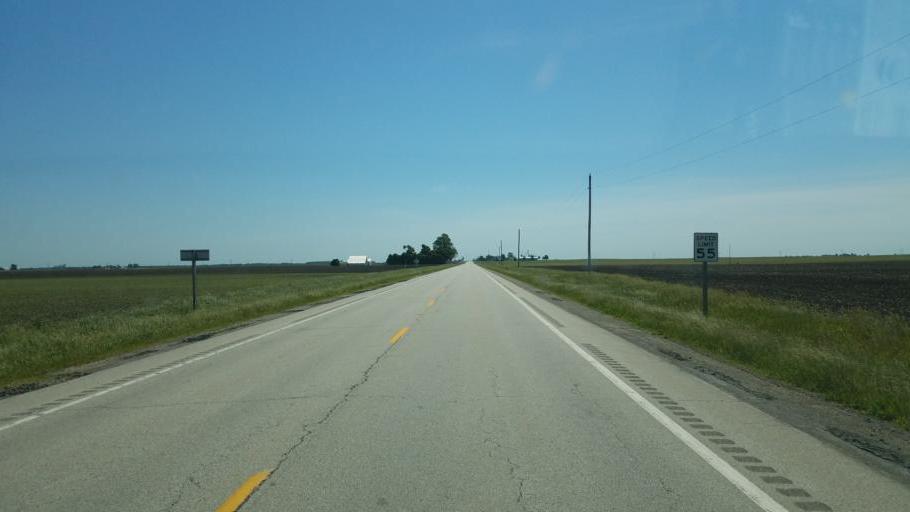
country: US
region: Illinois
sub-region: McLean County
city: Downs
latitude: 40.3121
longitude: -88.8617
